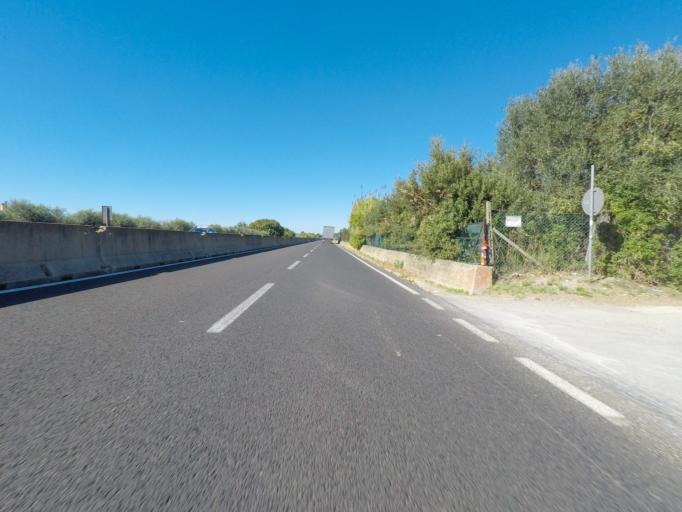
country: IT
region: Tuscany
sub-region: Provincia di Grosseto
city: Orbetello Scalo
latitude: 42.4603
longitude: 11.2461
